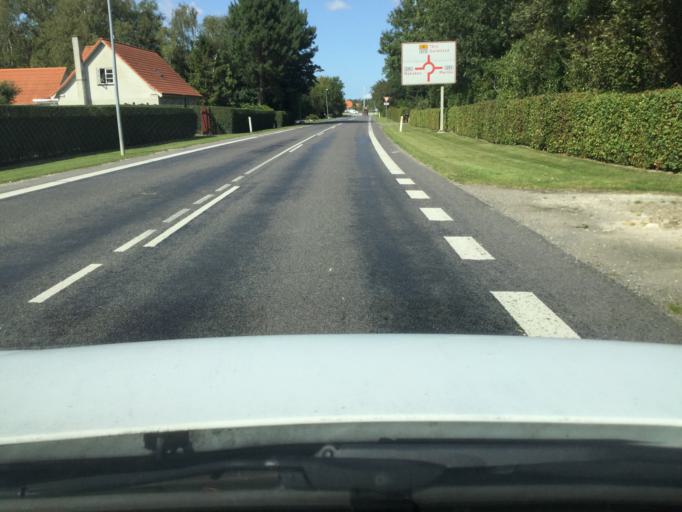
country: DK
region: Zealand
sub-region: Lolland Kommune
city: Nakskov
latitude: 54.7998
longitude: 11.2732
